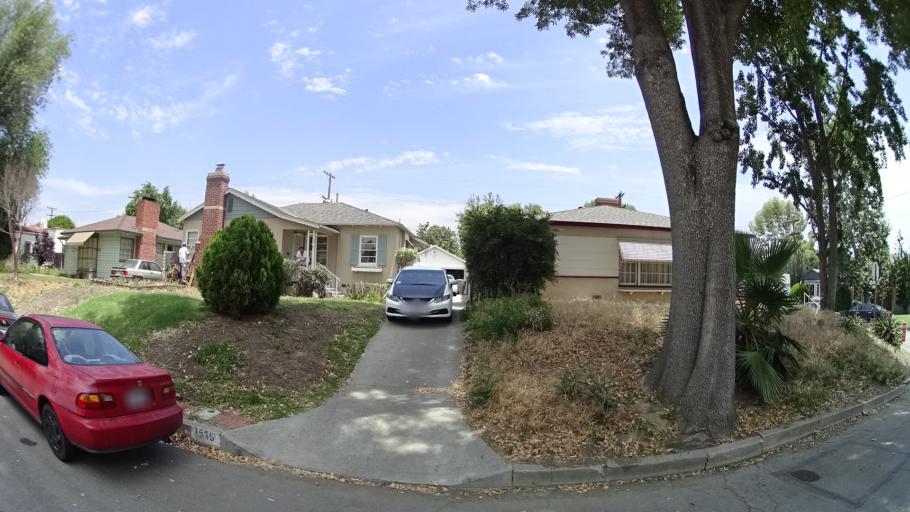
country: US
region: California
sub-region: Los Angeles County
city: Burbank
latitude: 34.1598
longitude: -118.2968
